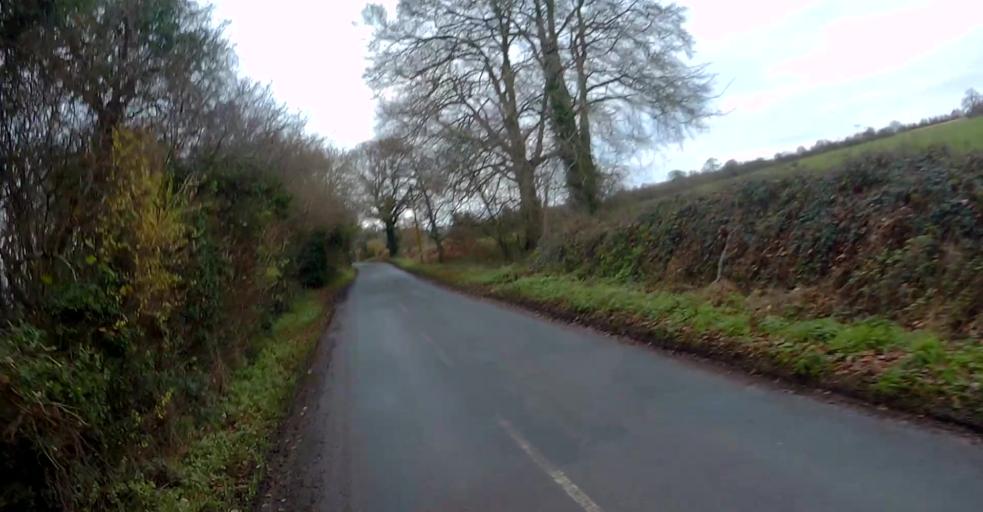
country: GB
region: England
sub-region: Hampshire
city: Basingstoke
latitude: 51.1899
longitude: -1.1555
